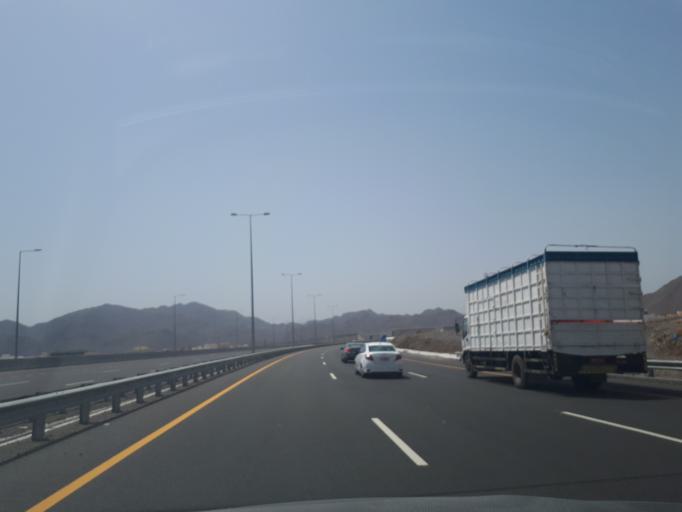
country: OM
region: Muhafazat ad Dakhiliyah
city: Bidbid
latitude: 23.3349
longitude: 58.1125
